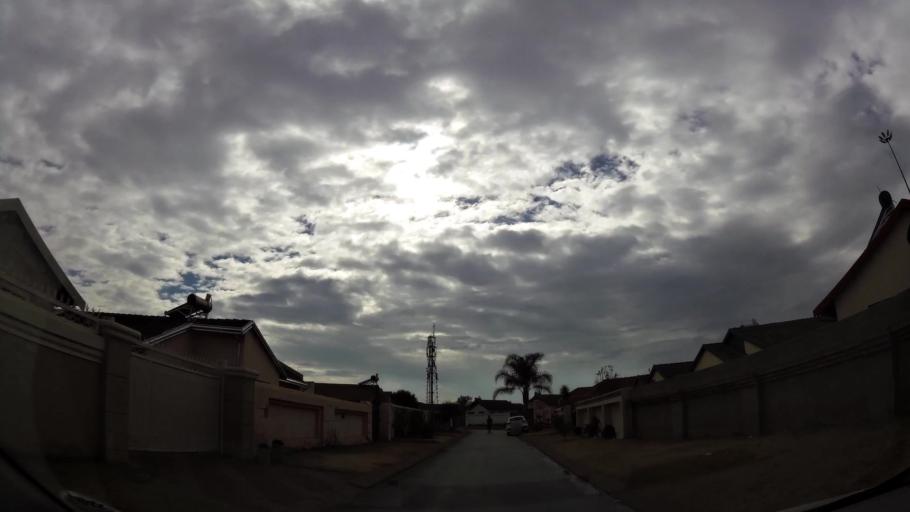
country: ZA
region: Gauteng
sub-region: Ekurhuleni Metropolitan Municipality
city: Germiston
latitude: -26.3330
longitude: 28.1959
